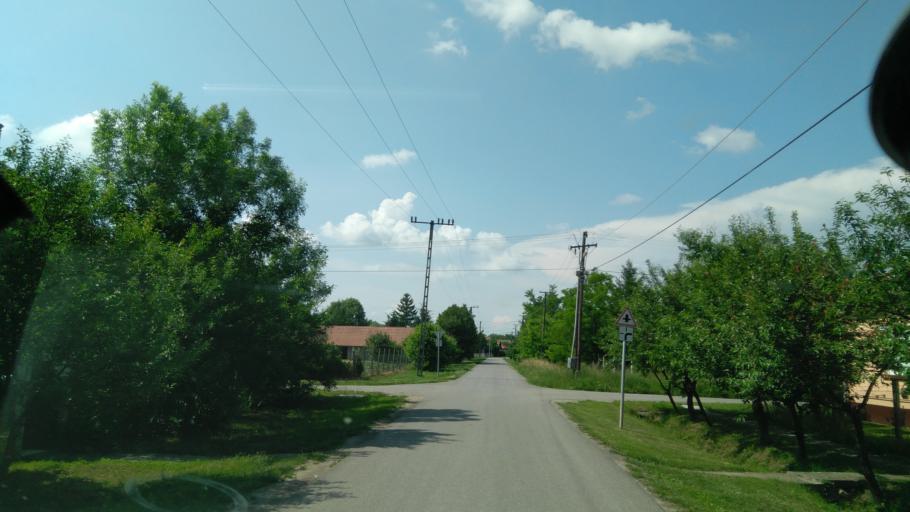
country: HU
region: Bekes
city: Doboz
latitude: 46.7351
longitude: 21.2307
